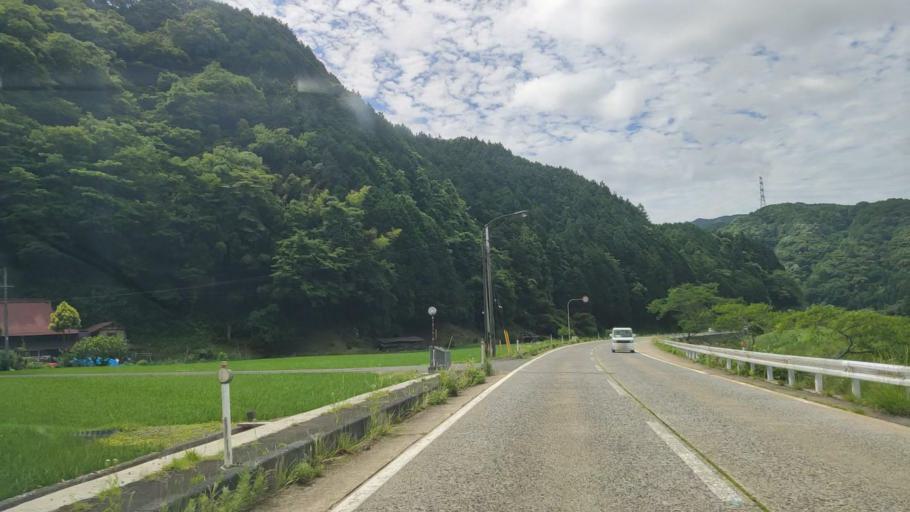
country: JP
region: Okayama
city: Niimi
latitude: 35.1689
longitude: 133.5798
